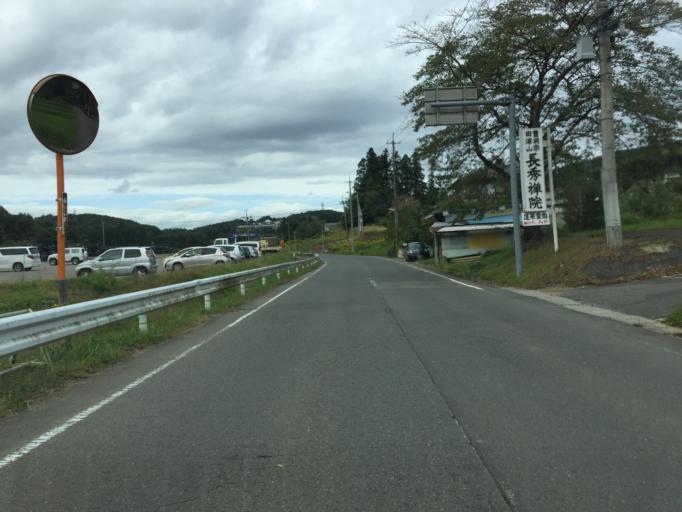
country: JP
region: Fukushima
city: Fukushima-shi
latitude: 37.6982
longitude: 140.4892
